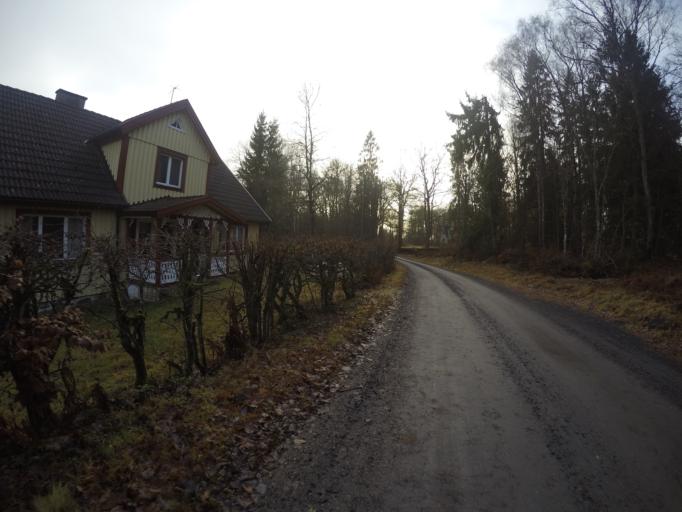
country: SE
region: Skane
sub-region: Osby Kommun
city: Lonsboda
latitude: 56.3735
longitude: 14.3368
